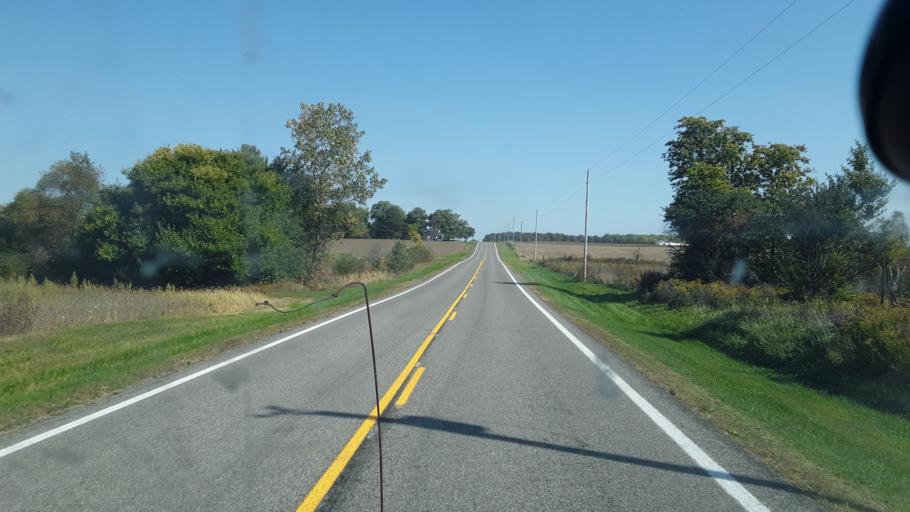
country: US
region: Ohio
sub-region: Logan County
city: Northwood
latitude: 40.5070
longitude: -83.6645
